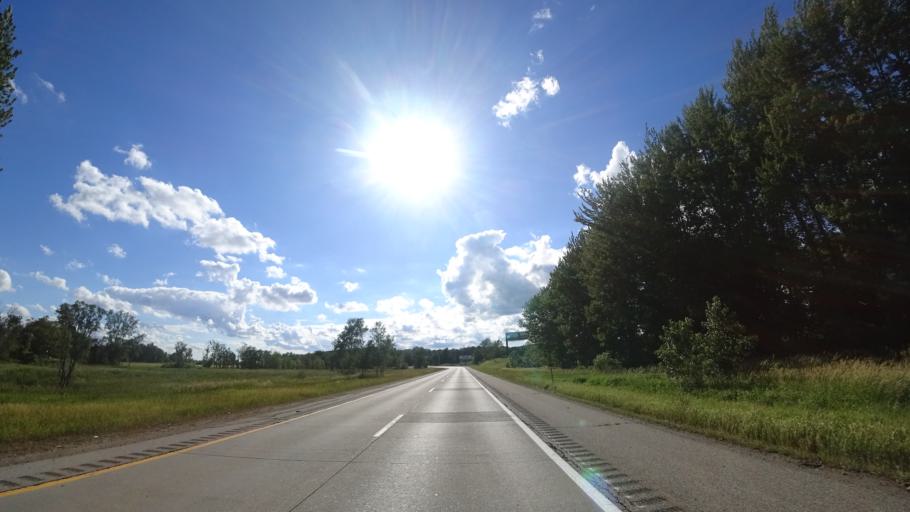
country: US
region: Michigan
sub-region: Ionia County
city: Saranac
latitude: 42.8798
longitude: -85.2768
